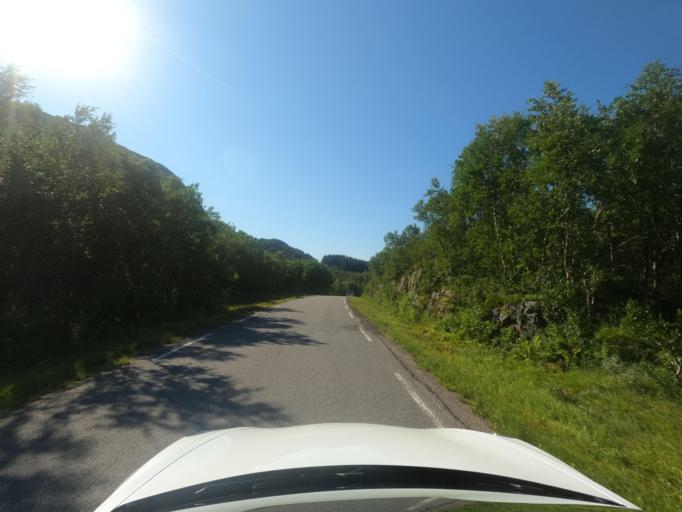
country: NO
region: Nordland
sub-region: Hadsel
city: Stokmarknes
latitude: 68.3213
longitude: 15.0048
